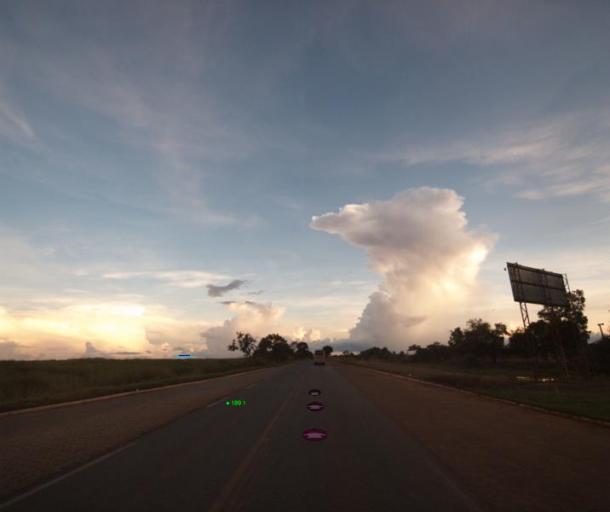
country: BR
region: Goias
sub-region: Uruacu
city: Uruacu
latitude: -14.4310
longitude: -49.1569
